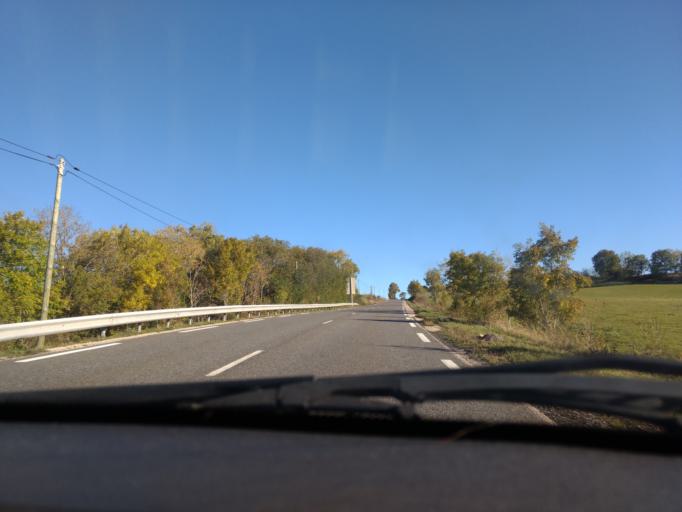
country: FR
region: Midi-Pyrenees
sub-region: Departement de l'Aveyron
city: Laguiole
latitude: 44.7092
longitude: 2.8585
